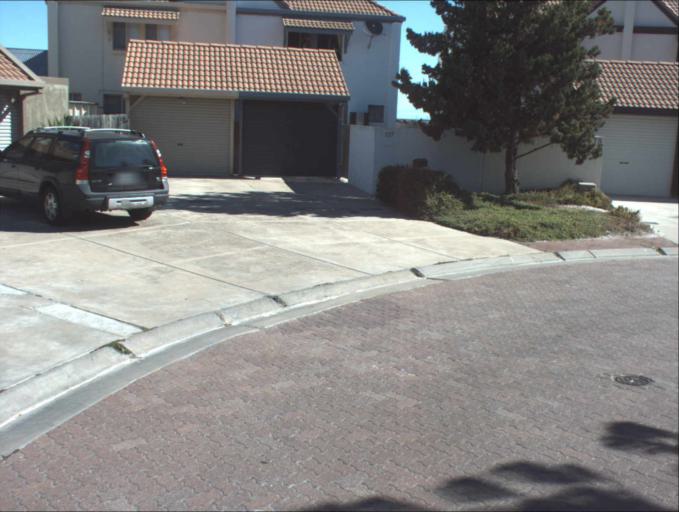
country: AU
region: South Australia
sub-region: Port Adelaide Enfield
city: Birkenhead
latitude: -34.7905
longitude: 138.4860
